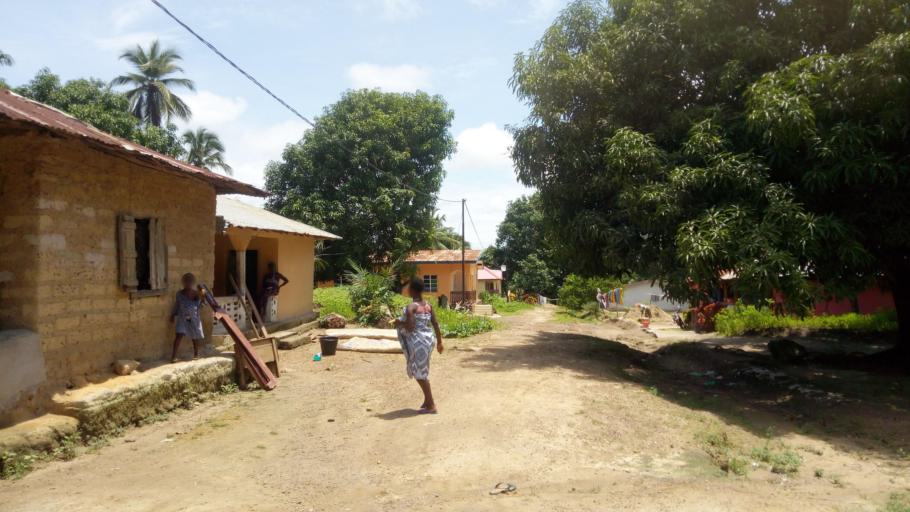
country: SL
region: Northern Province
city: Magburaka
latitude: 8.7194
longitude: -11.9576
